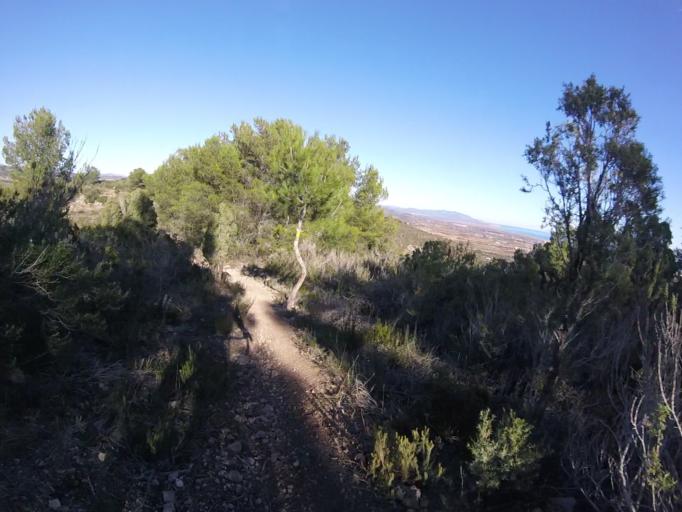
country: ES
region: Valencia
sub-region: Provincia de Castello
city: Orpesa/Oropesa del Mar
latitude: 40.1132
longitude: 0.1169
